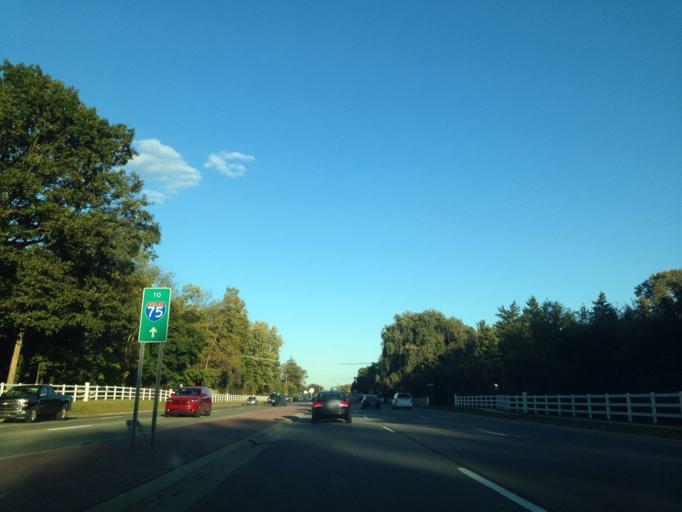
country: US
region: Michigan
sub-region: Oakland County
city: Bloomfield Hills
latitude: 42.6034
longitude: -83.2728
